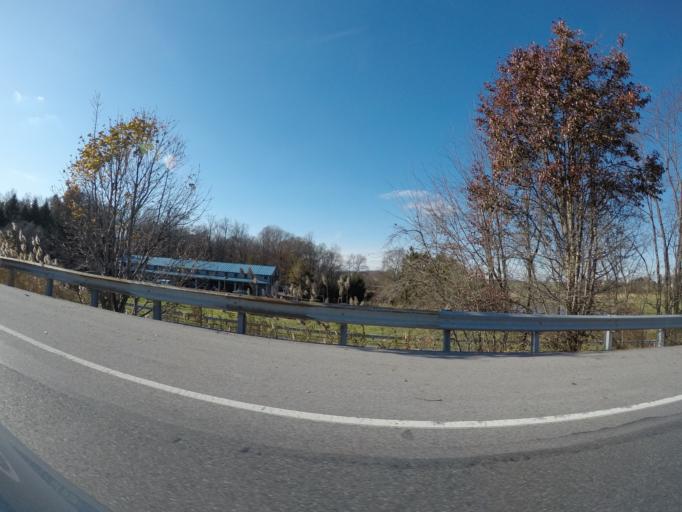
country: US
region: Pennsylvania
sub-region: Chester County
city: Oxford
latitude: 39.8076
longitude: -75.9689
